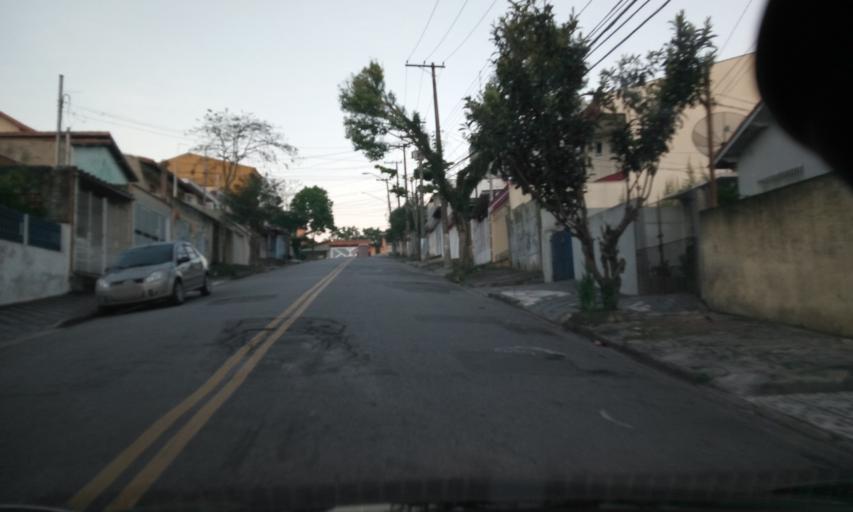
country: BR
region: Sao Paulo
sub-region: Sao Bernardo Do Campo
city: Sao Bernardo do Campo
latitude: -23.7263
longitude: -46.5686
